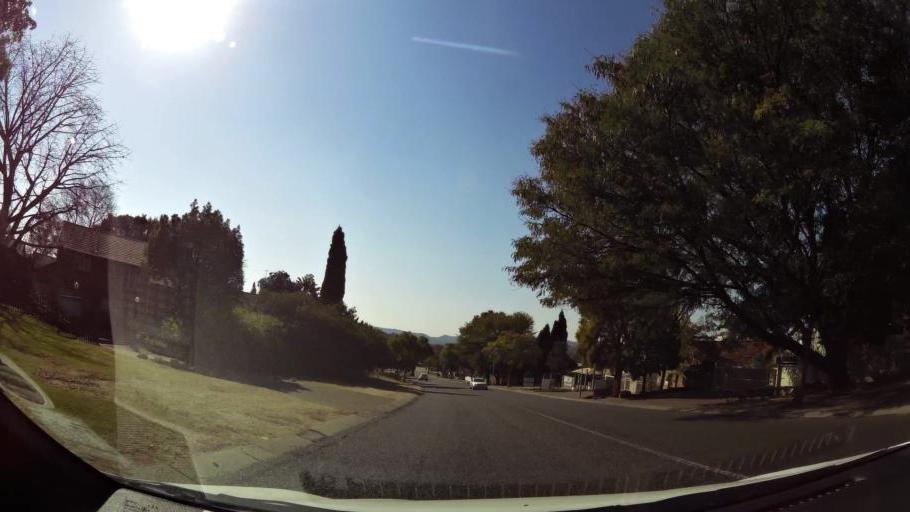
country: ZA
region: Gauteng
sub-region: City of Tshwane Metropolitan Municipality
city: Centurion
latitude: -25.8167
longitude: 28.2949
